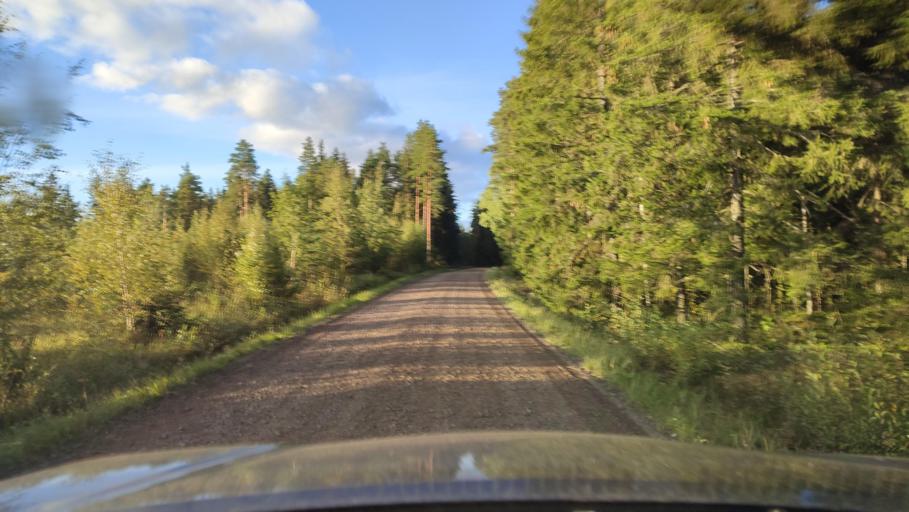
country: FI
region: Southern Ostrobothnia
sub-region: Suupohja
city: Karijoki
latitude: 62.2276
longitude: 21.5724
